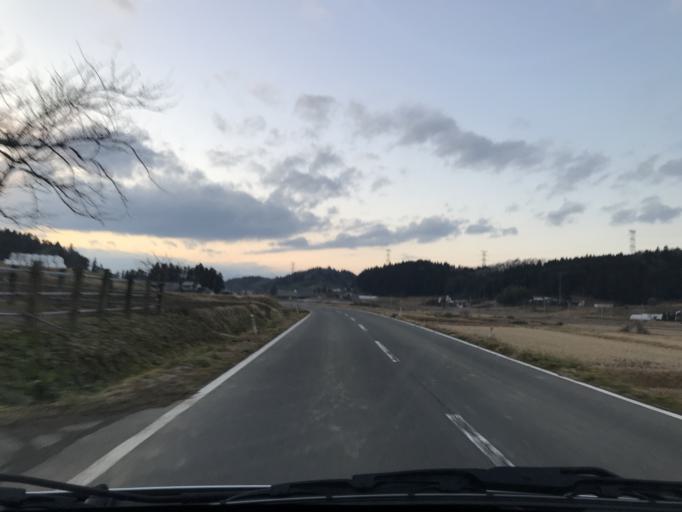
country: JP
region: Iwate
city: Ichinoseki
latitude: 38.8472
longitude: 141.1067
